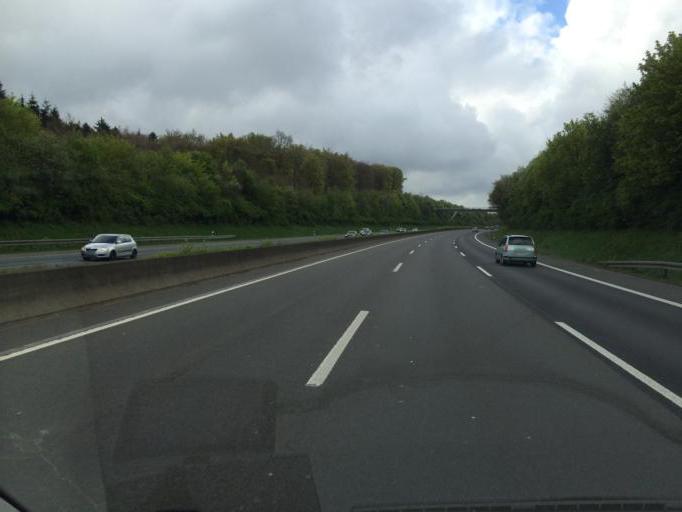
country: DE
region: North Rhine-Westphalia
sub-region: Regierungsbezirk Dusseldorf
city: Remscheid
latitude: 51.2164
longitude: 7.2509
